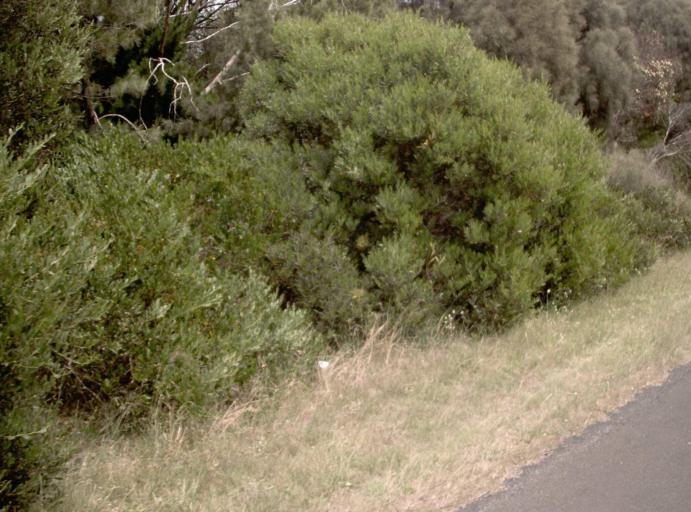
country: AU
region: Victoria
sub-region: Mornington Peninsula
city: Rosebud
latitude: -38.3733
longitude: 144.8989
